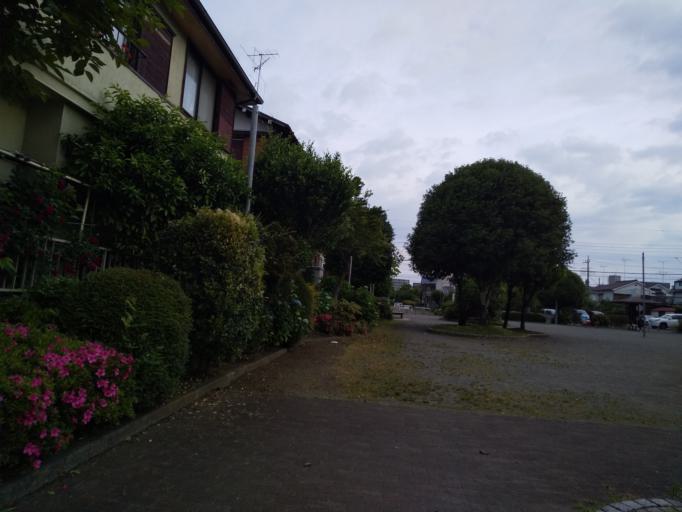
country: JP
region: Kanagawa
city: Zama
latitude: 35.5605
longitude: 139.3806
